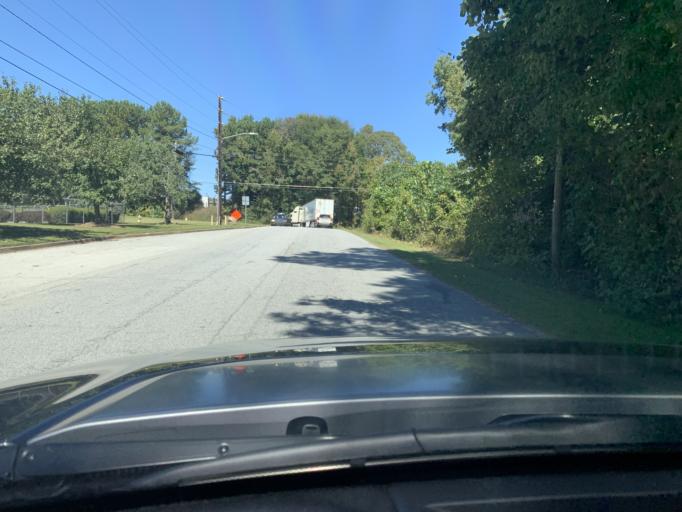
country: US
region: Georgia
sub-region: Clayton County
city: Conley
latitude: 33.6658
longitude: -84.3272
